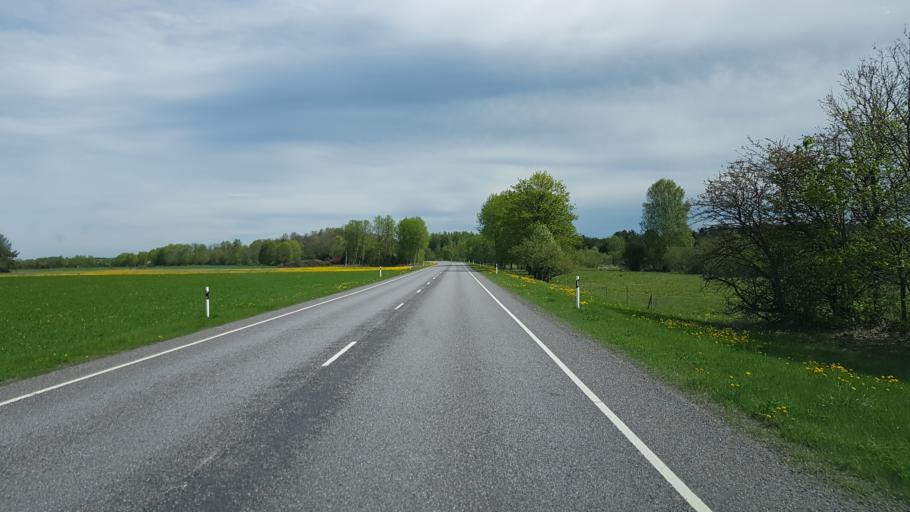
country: EE
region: Saare
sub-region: Kuressaare linn
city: Kuressaare
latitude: 58.3587
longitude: 22.7130
